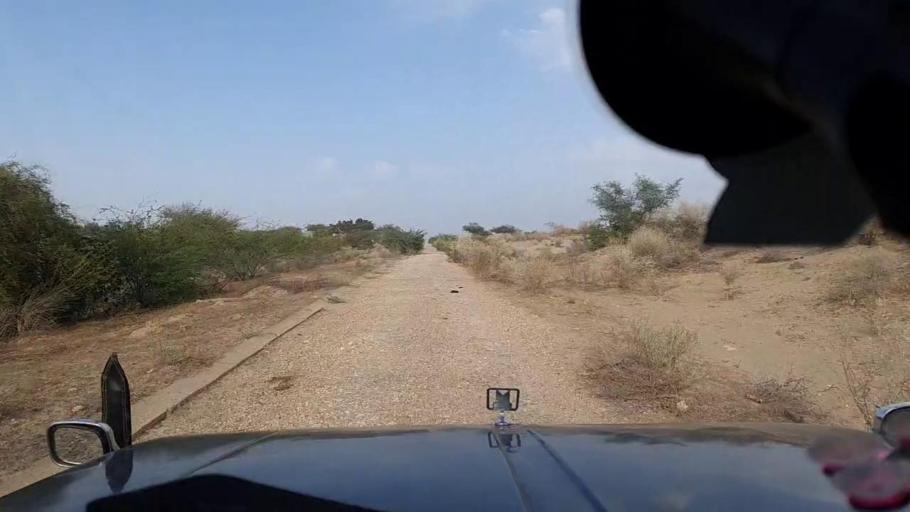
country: PK
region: Sindh
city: Diplo
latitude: 24.5401
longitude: 69.4668
